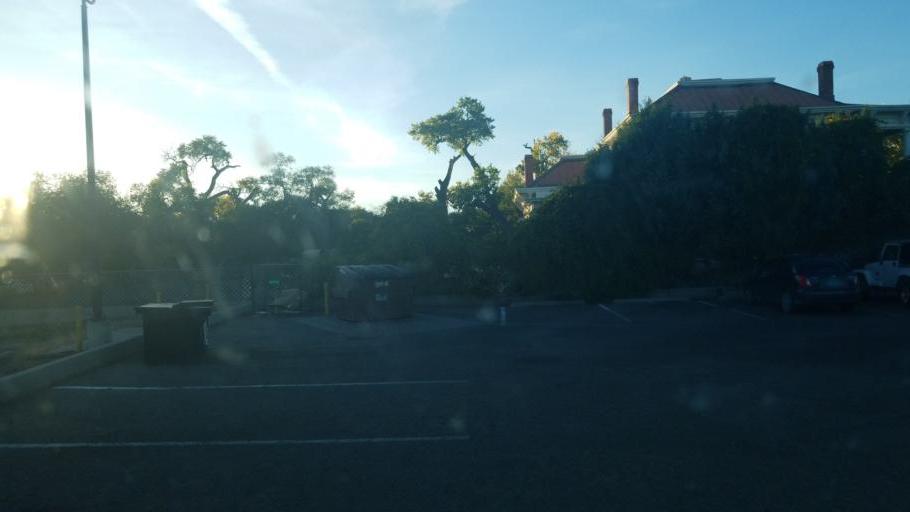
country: US
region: New Mexico
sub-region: Valencia County
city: Los Lunas
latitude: 34.8072
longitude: -106.7364
